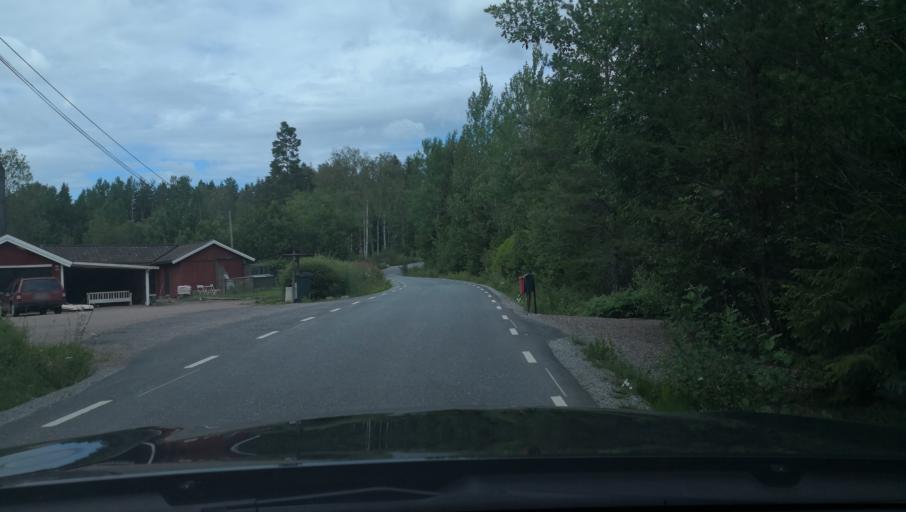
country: SE
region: Vaestmanland
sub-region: Hallstahammars Kommun
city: Hallstahammar
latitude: 59.6233
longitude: 16.1424
